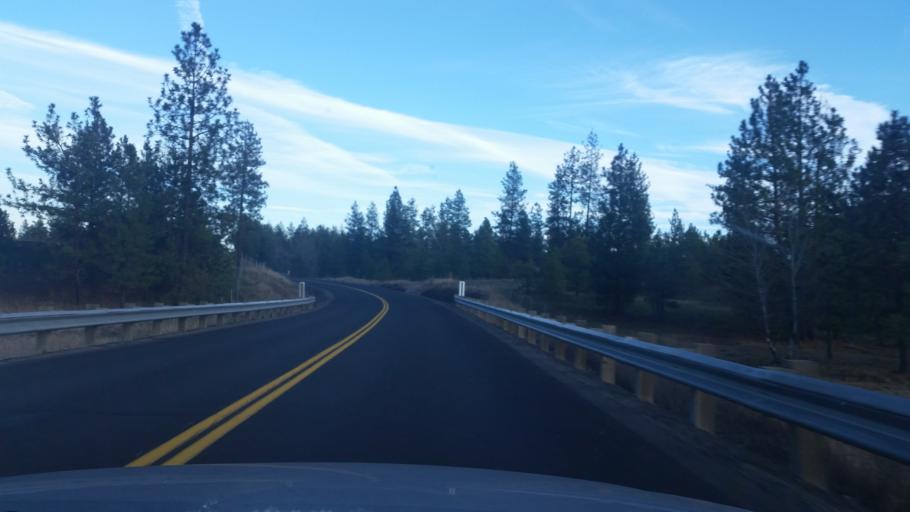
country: US
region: Washington
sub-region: Spokane County
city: Cheney
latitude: 47.4808
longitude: -117.5089
